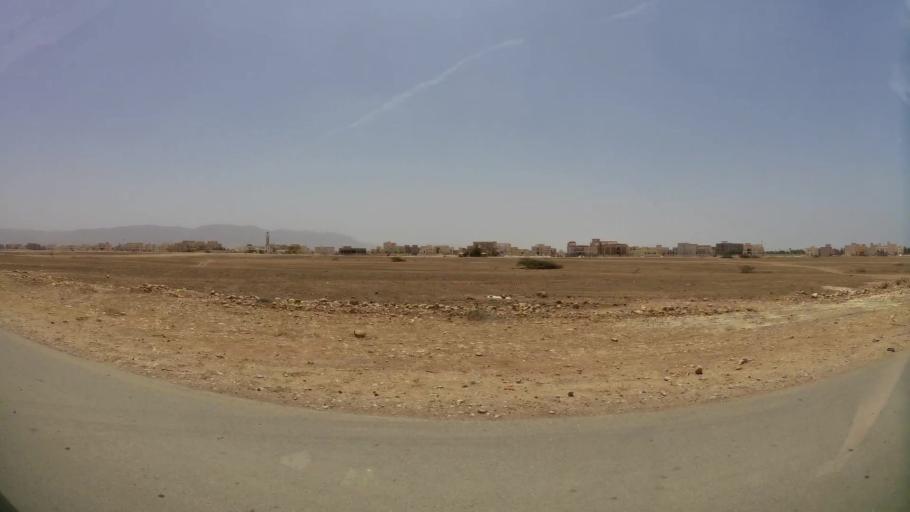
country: OM
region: Zufar
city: Salalah
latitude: 17.0537
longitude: 54.2076
